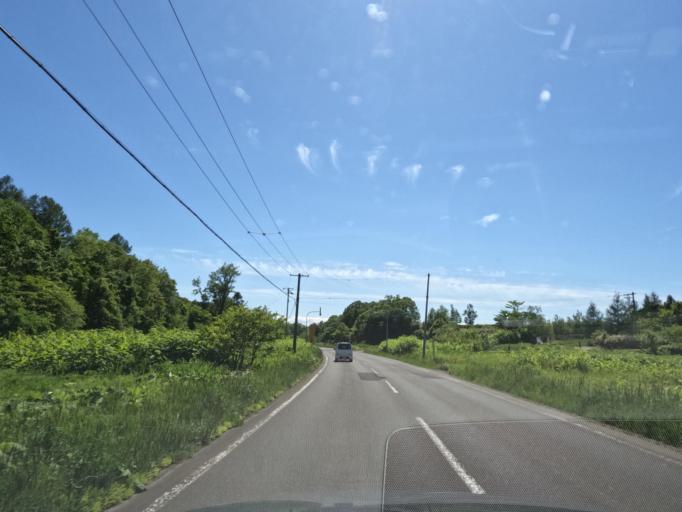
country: JP
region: Hokkaido
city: Iwamizawa
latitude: 43.0986
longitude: 141.7676
